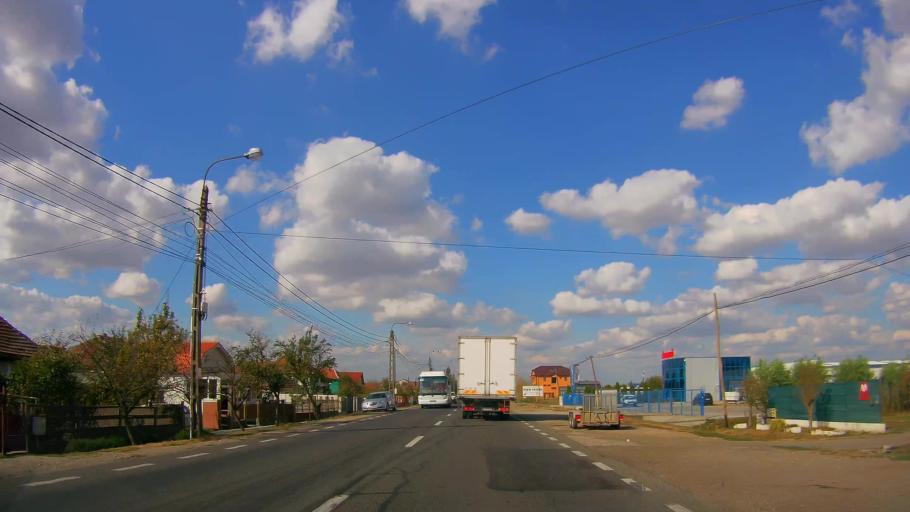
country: RO
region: Satu Mare
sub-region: Comuna Paulesti
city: Paulesti
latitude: 47.7504
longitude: 22.8831
